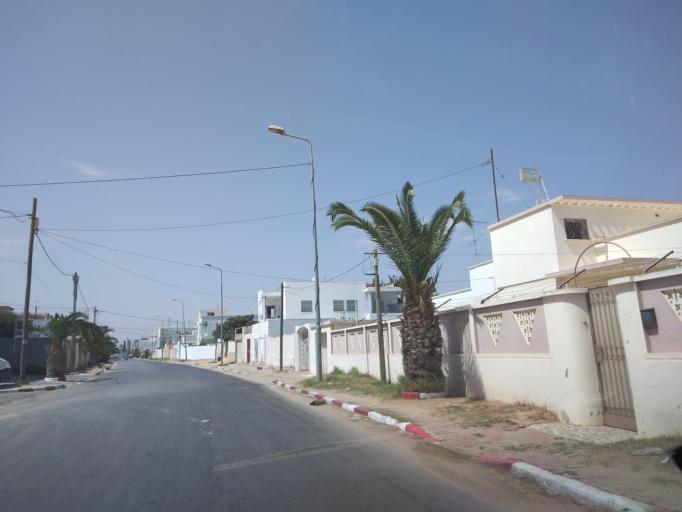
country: TN
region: Safaqis
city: Sfax
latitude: 34.7569
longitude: 10.7525
